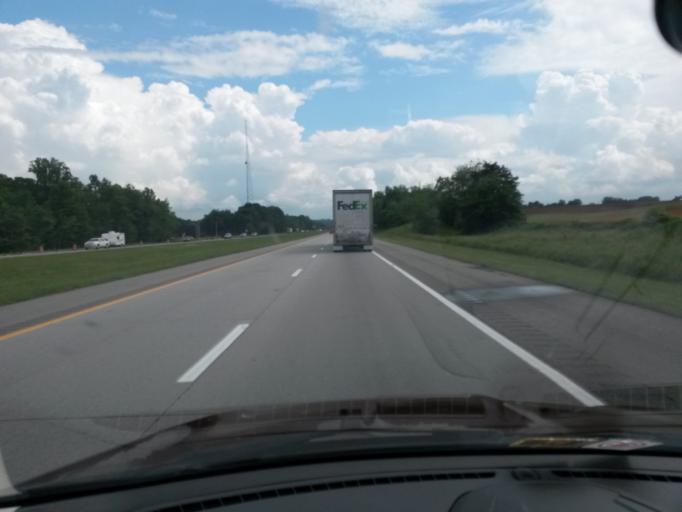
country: US
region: North Carolina
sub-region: Yadkin County
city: Jonesville
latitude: 36.1107
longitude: -80.8140
